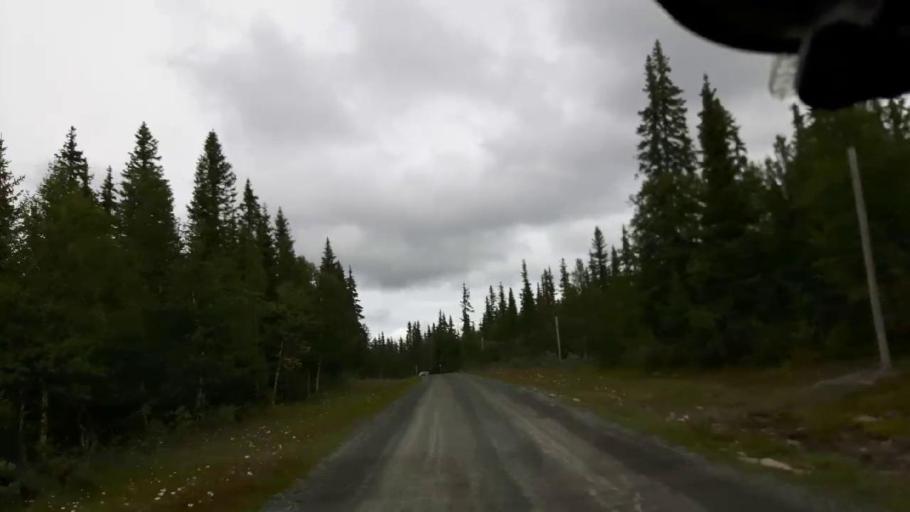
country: SE
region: Jaemtland
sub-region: Krokoms Kommun
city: Valla
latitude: 63.7624
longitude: 13.8371
